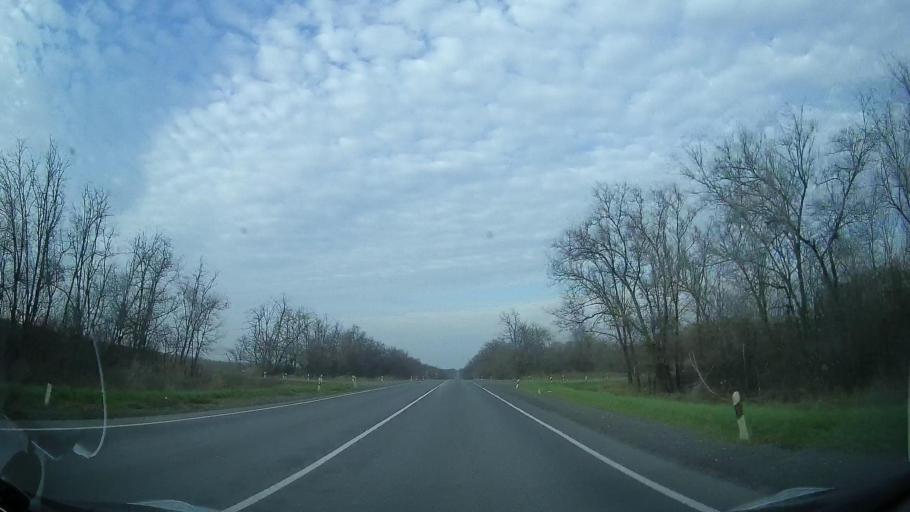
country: RU
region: Rostov
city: Bagayevskaya
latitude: 47.1033
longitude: 40.2767
